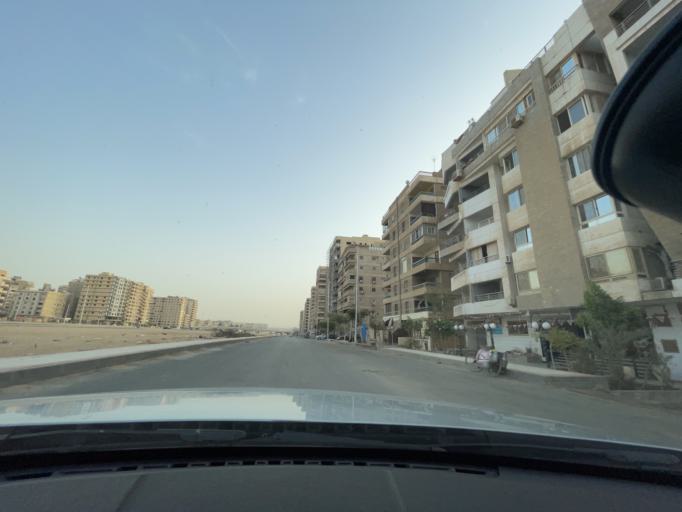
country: EG
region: Muhafazat al Qahirah
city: Cairo
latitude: 30.0521
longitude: 31.3693
